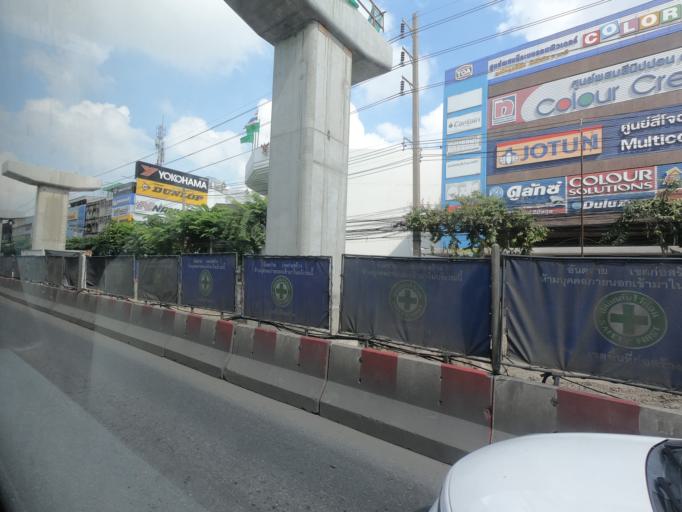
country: TH
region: Bangkok
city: Wang Thonglang
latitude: 13.7887
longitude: 100.6046
